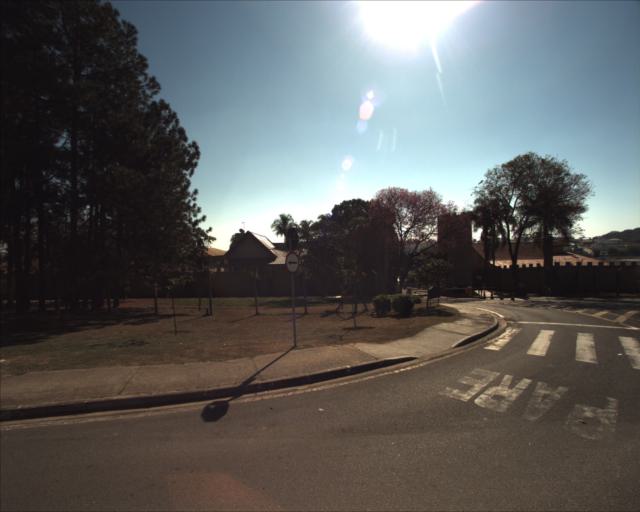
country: BR
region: Sao Paulo
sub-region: Sorocaba
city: Sorocaba
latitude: -23.4936
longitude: -47.4070
